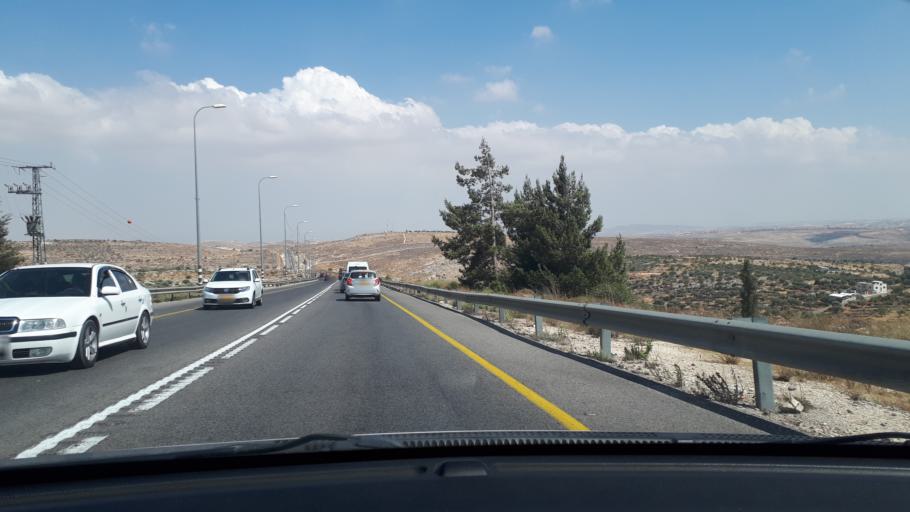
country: PS
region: West Bank
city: Burqah
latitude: 31.9040
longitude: 35.2574
